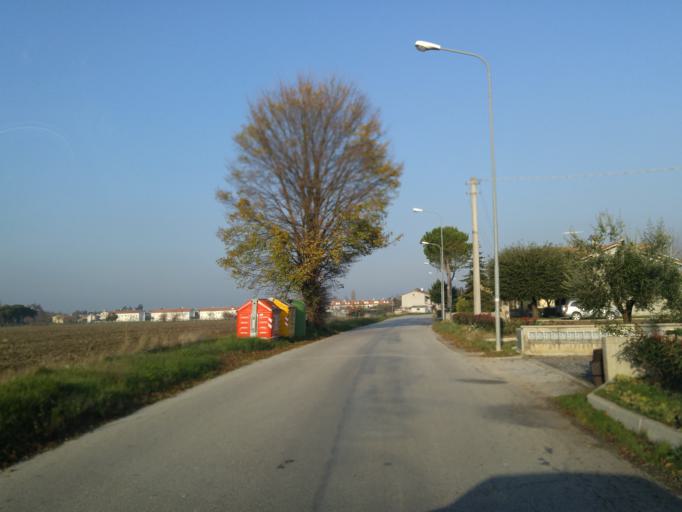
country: IT
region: The Marches
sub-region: Provincia di Pesaro e Urbino
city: Bellocchi
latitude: 43.7927
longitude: 12.9915
